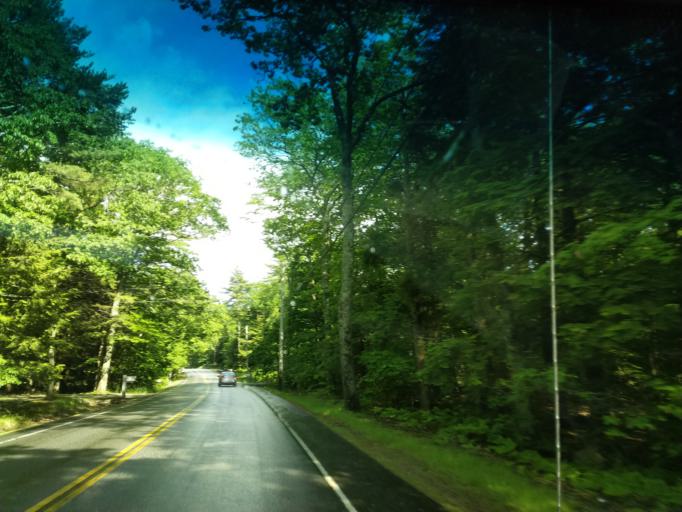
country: US
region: Maine
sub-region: Cumberland County
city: Falmouth
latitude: 43.7477
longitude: -70.3100
